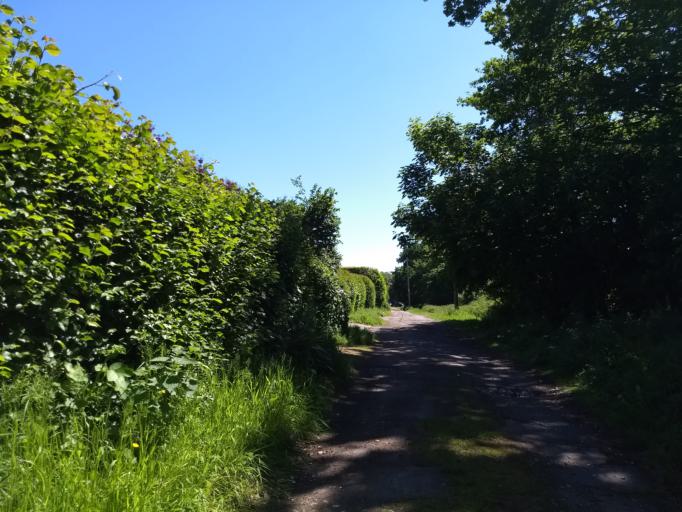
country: GB
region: England
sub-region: Isle of Wight
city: Seaview
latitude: 50.6988
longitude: -1.1170
